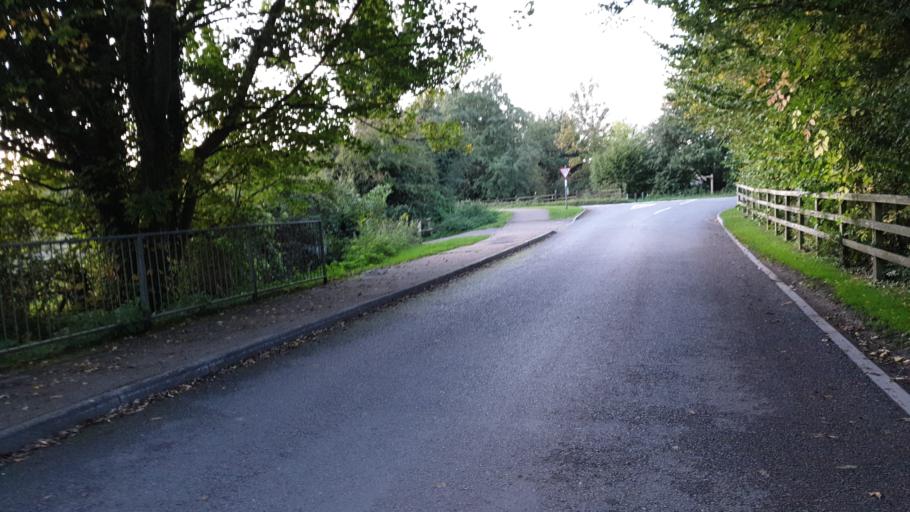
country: GB
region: England
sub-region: Wiltshire
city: Minety
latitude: 51.6504
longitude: -1.9705
